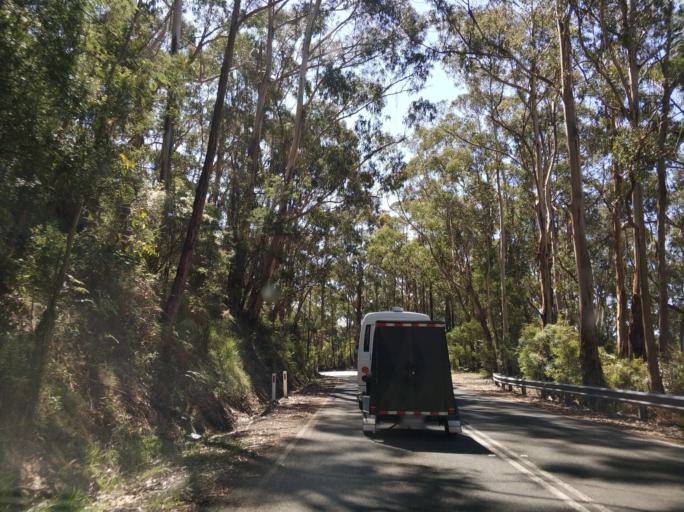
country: AU
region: Victoria
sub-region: Colac-Otway
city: Apollo Bay
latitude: -38.7427
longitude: 143.2545
